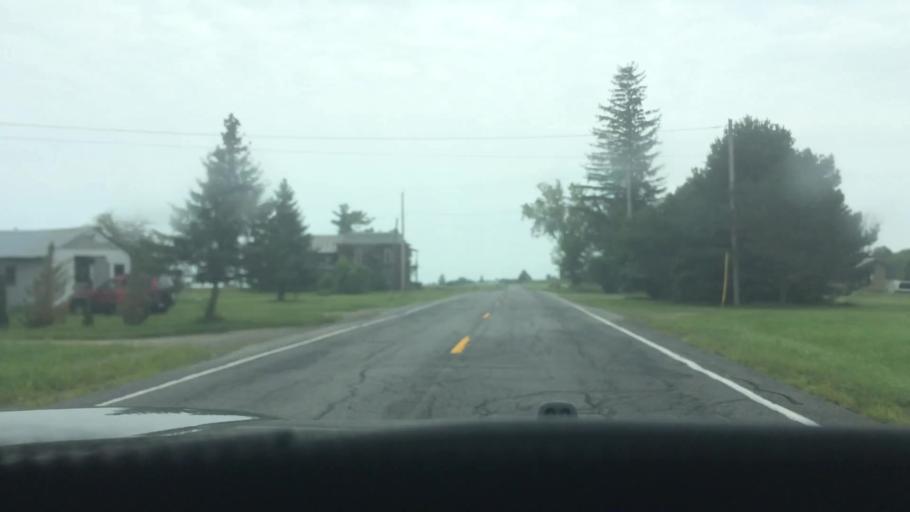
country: US
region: New York
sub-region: St. Lawrence County
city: Hannawa Falls
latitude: 44.6816
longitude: -74.7177
